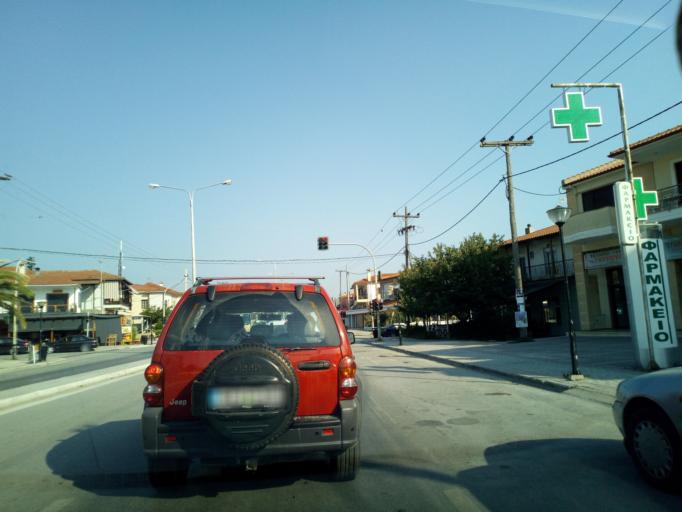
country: GR
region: Central Macedonia
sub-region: Nomos Chalkidikis
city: Nikiti
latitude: 40.2230
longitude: 23.6686
